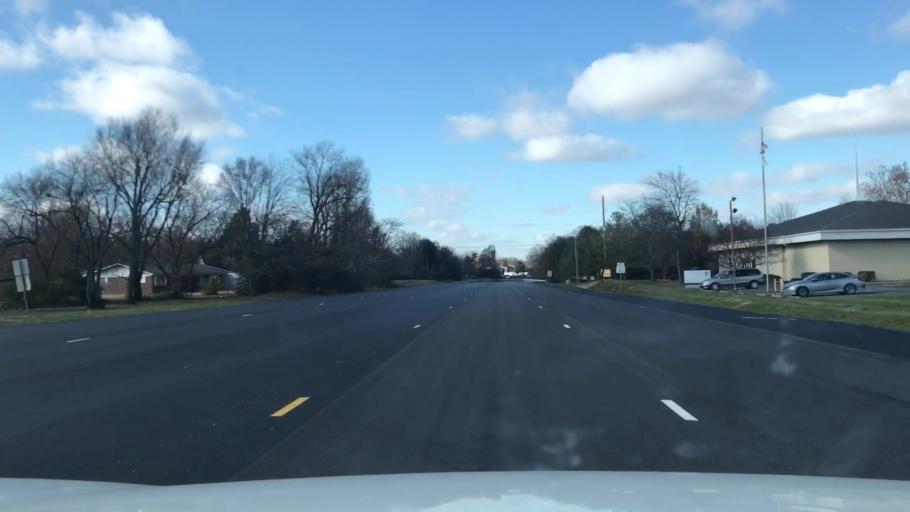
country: US
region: Illinois
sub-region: Saint Clair County
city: Swansea
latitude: 38.5512
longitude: -90.0118
